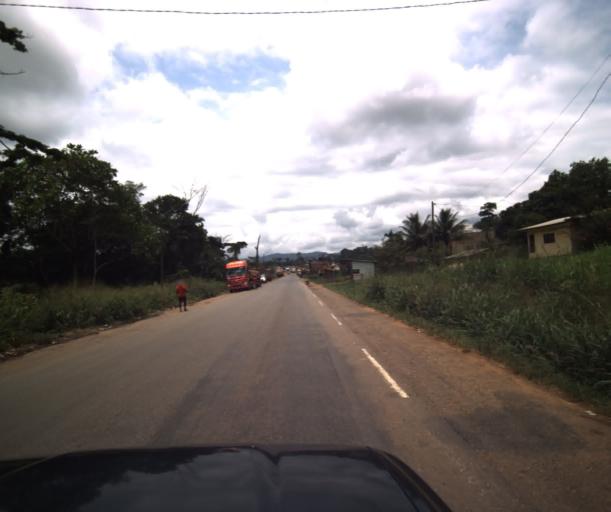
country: CM
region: Centre
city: Eseka
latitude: 3.8821
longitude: 10.8527
